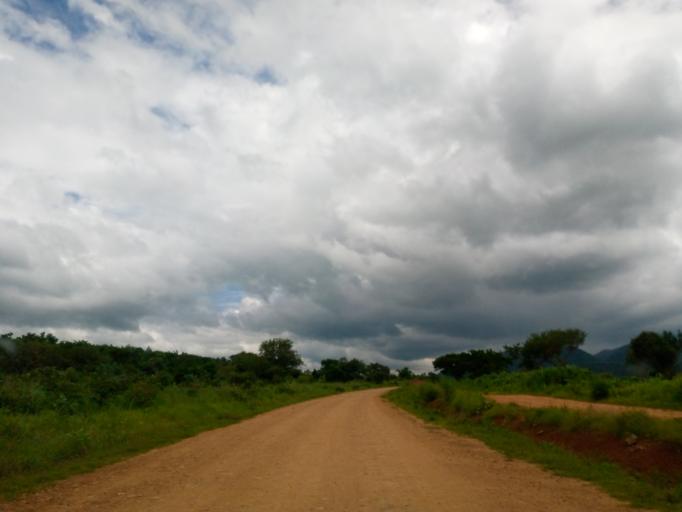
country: ET
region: Oromiya
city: Mendi
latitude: 10.1932
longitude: 35.0931
